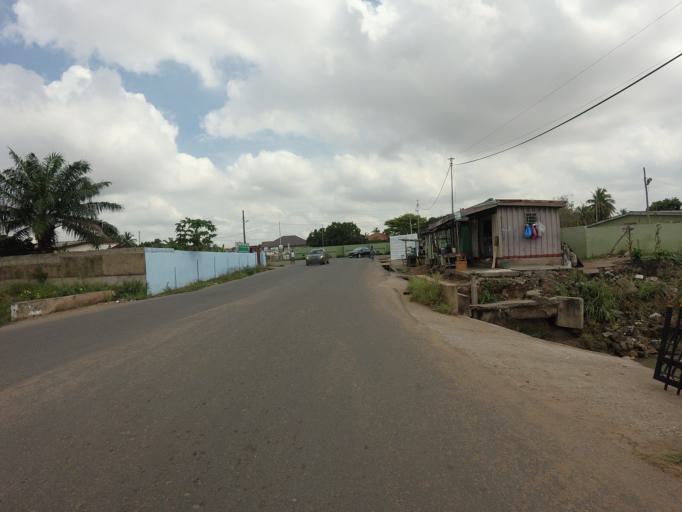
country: GH
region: Greater Accra
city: Nungua
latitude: 5.6174
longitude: -0.0853
